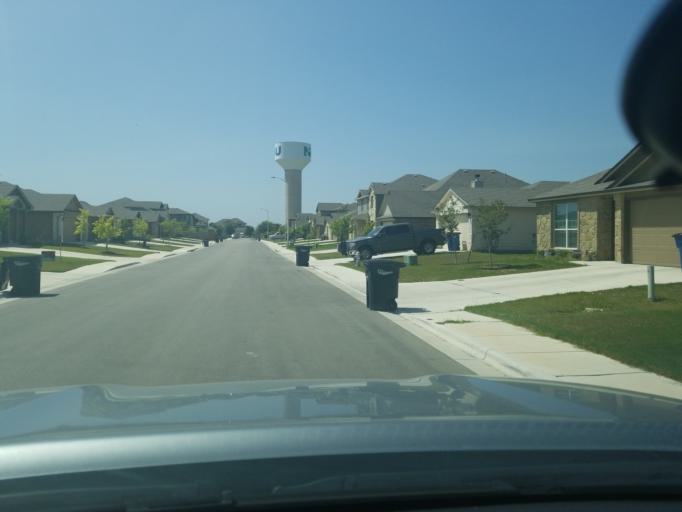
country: US
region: Texas
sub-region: Guadalupe County
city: Lake Dunlap
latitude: 29.6750
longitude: -98.0340
